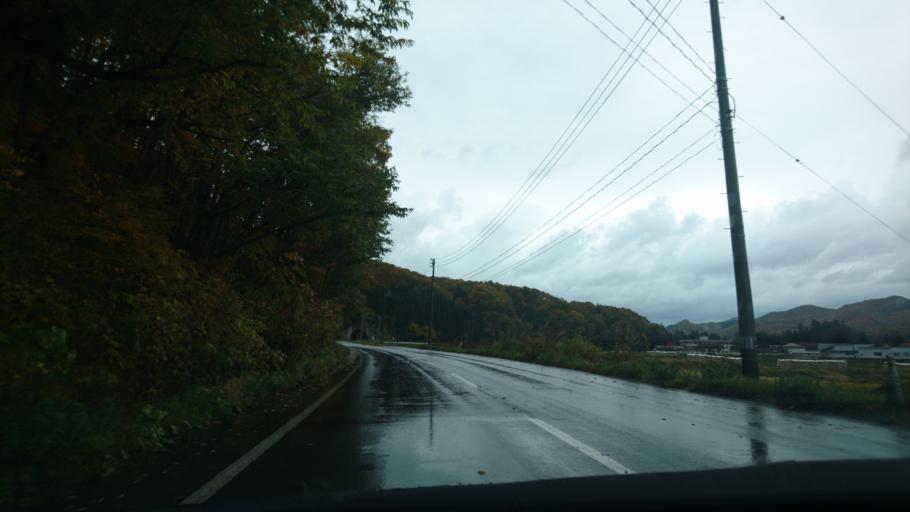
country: JP
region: Akita
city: Yokotemachi
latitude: 39.3494
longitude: 140.7653
